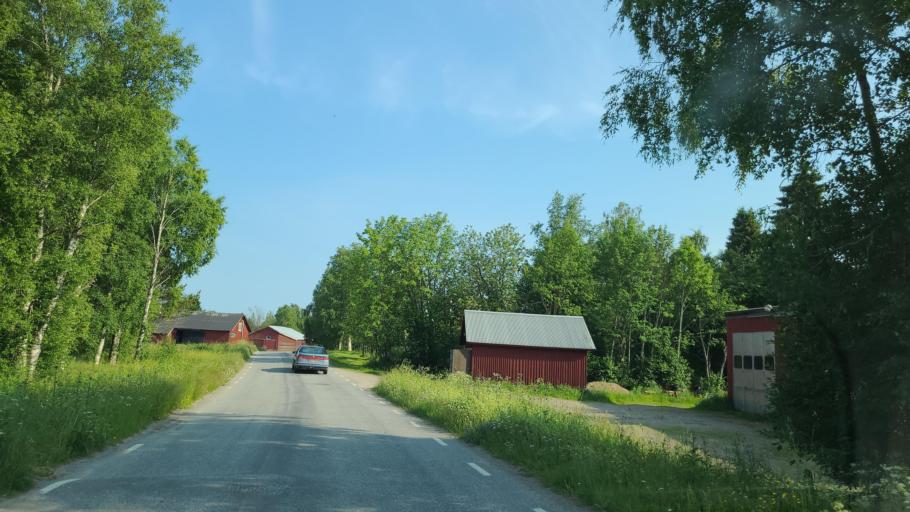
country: SE
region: Vaesterbotten
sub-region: Skelleftea Kommun
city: Burea
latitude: 64.3482
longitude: 21.3375
